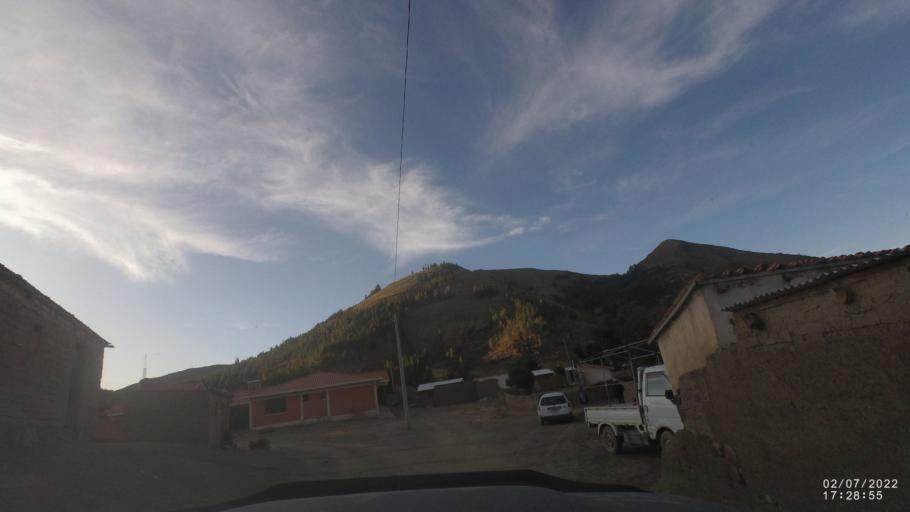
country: BO
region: Cochabamba
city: Irpa Irpa
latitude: -17.8821
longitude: -66.6168
